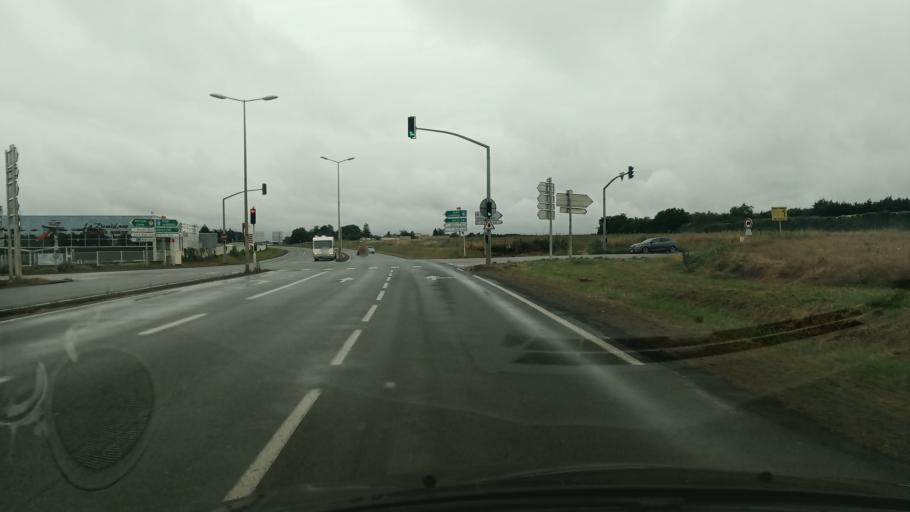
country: FR
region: Poitou-Charentes
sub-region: Departement de la Vienne
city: Poitiers
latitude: 46.6000
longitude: 0.3218
